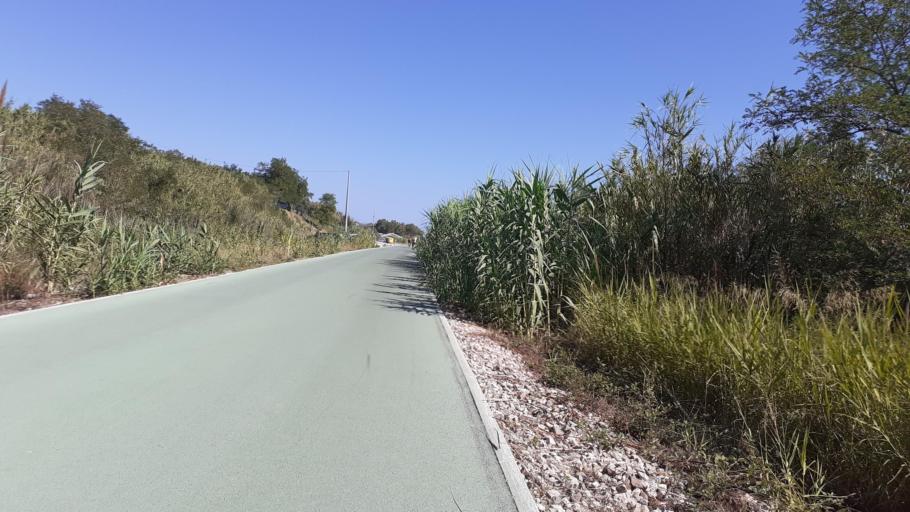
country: IT
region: Abruzzo
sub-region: Provincia di Chieti
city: Vasto
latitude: 42.1143
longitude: 14.7194
